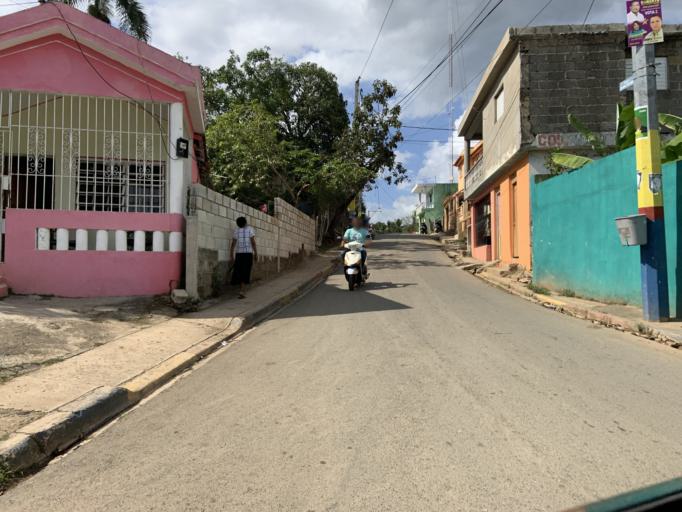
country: DO
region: Monte Plata
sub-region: Yamasa
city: Yamasa
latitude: 18.7760
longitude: -70.0287
